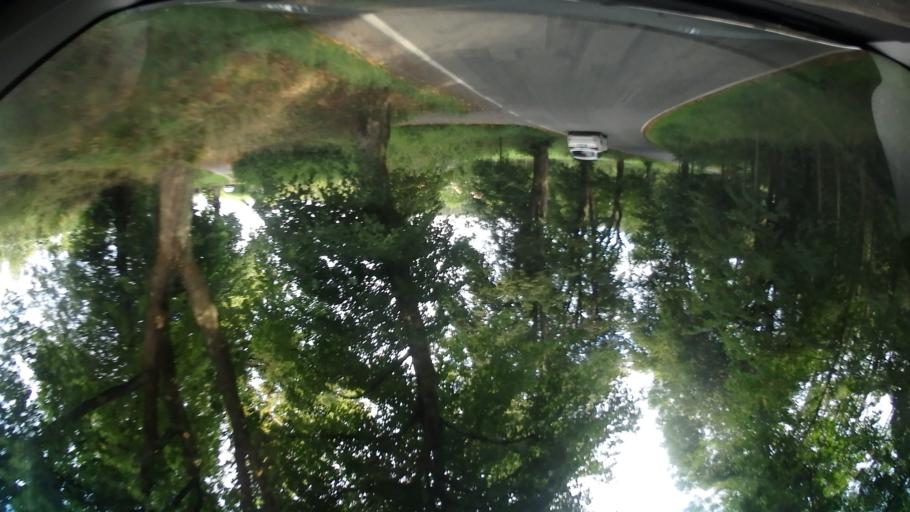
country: CZ
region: Olomoucky
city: Horni Stepanov
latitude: 49.5595
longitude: 16.7524
